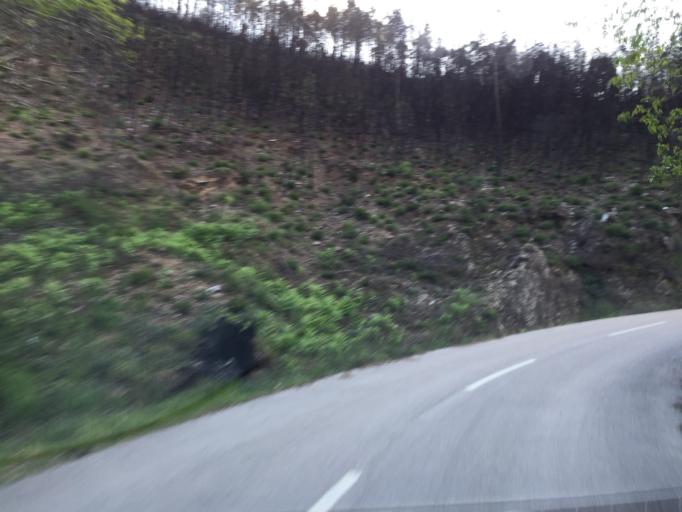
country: PT
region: Coimbra
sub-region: Arganil
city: Arganil
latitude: 40.1290
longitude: -8.0117
